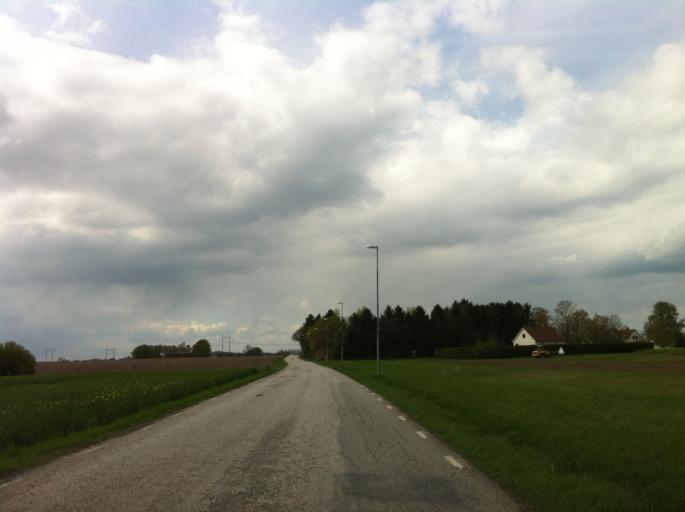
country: SE
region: Skane
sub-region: Kavlinge Kommun
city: Kaevlinge
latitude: 55.8121
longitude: 13.1416
